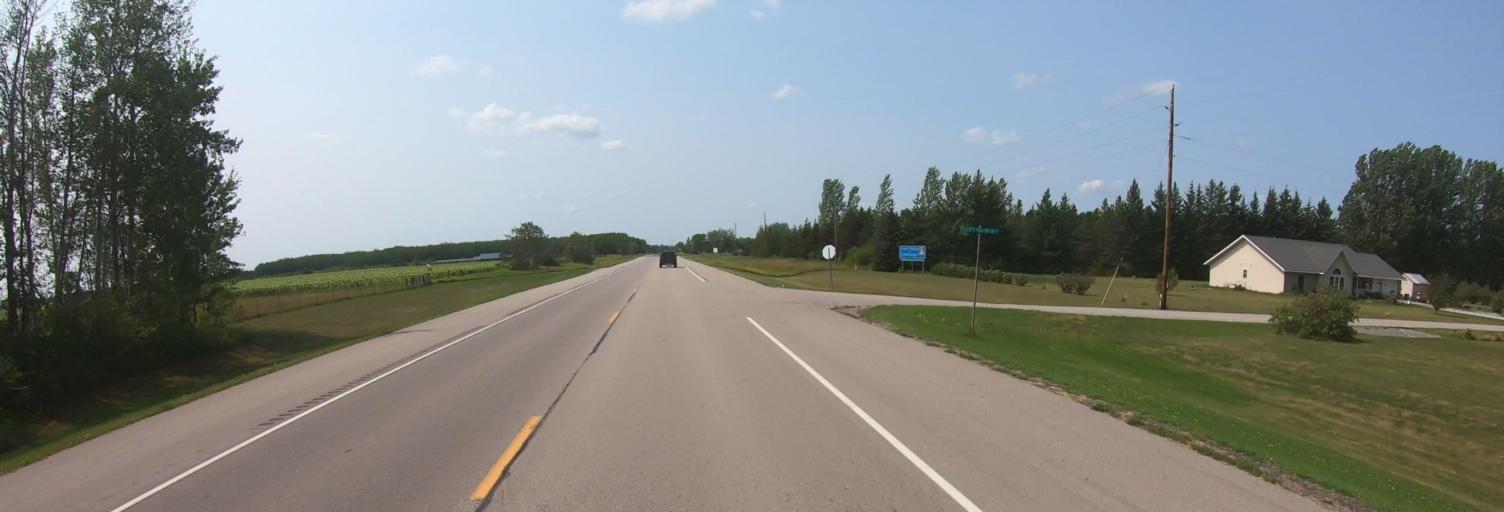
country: US
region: Minnesota
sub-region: Lake of the Woods County
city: Baudette
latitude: 48.7118
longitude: -94.5710
